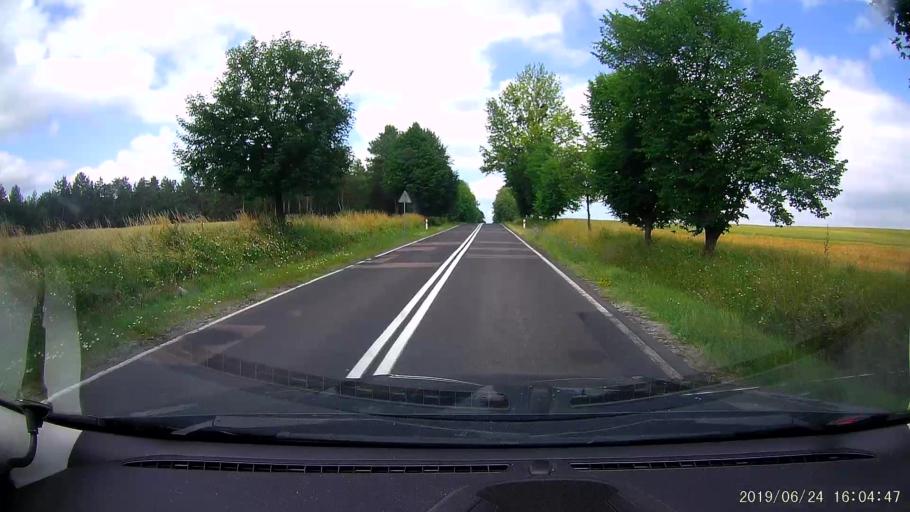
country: PL
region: Subcarpathian Voivodeship
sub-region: Powiat lubaczowski
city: Narol
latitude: 50.3209
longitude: 23.2703
